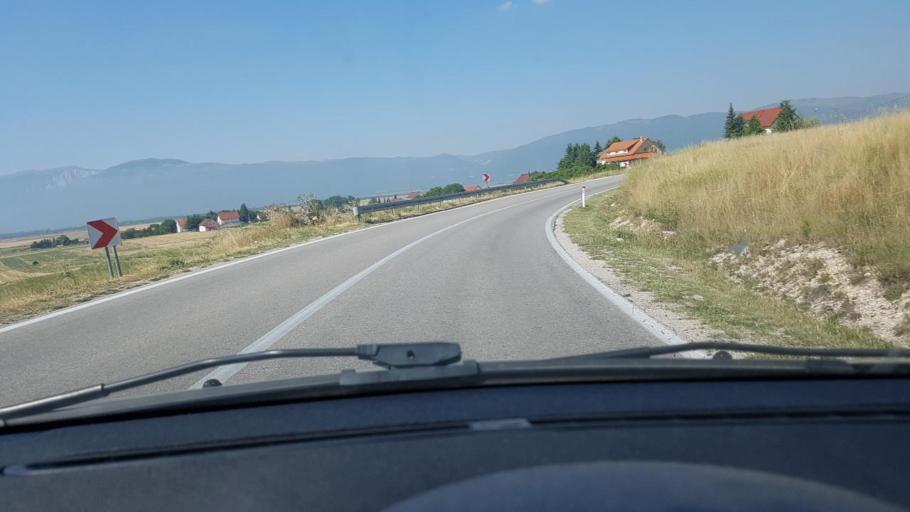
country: BA
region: Federation of Bosnia and Herzegovina
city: Zabrisce
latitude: 43.8606
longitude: 16.9017
